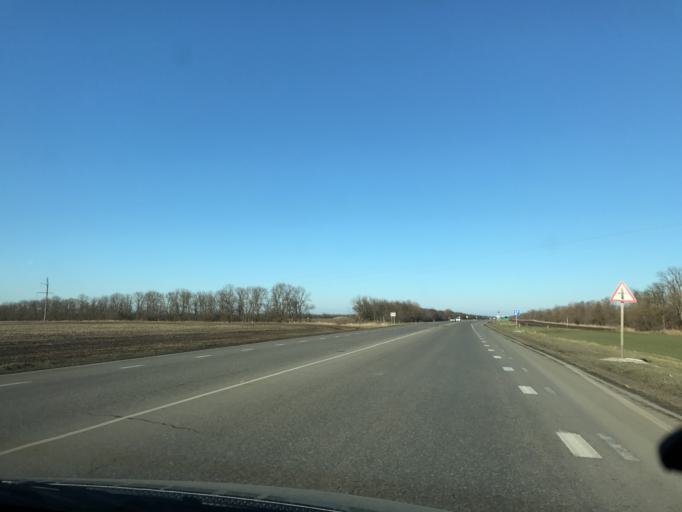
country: RU
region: Rostov
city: Kagal'nitskaya
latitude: 46.9280
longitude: 40.0984
